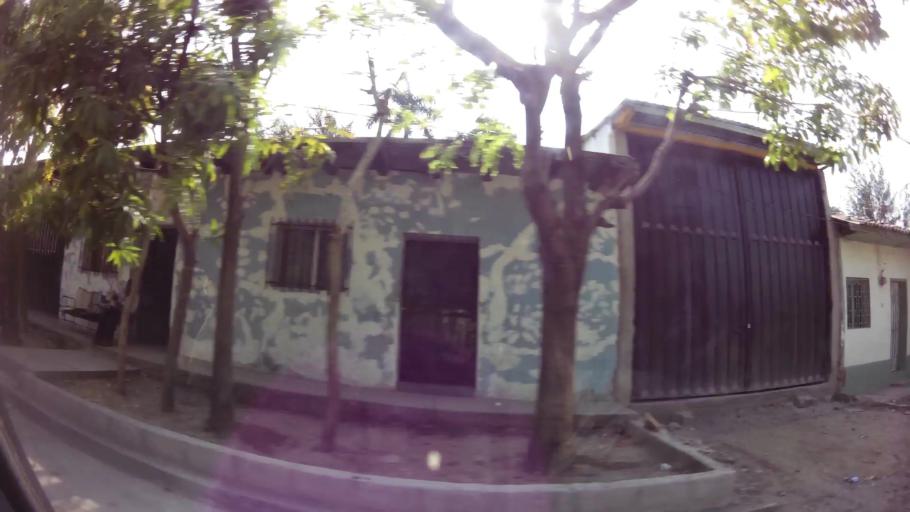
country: HN
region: Comayagua
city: Comayagua
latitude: 14.4508
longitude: -87.6388
